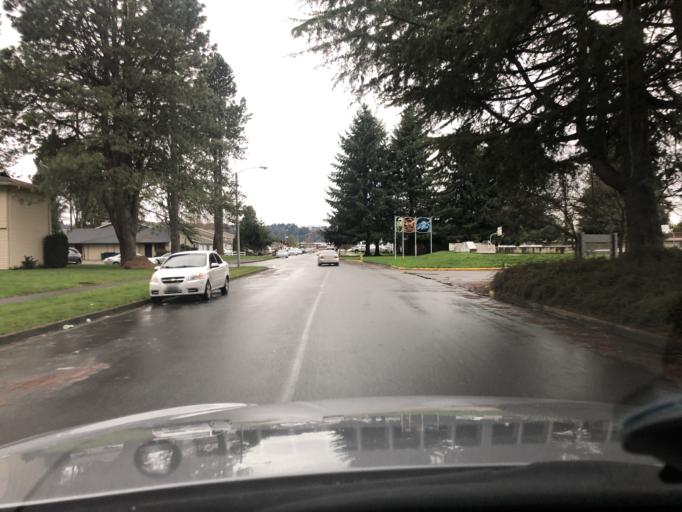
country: US
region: Washington
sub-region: King County
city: Auburn
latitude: 47.3319
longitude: -122.2157
